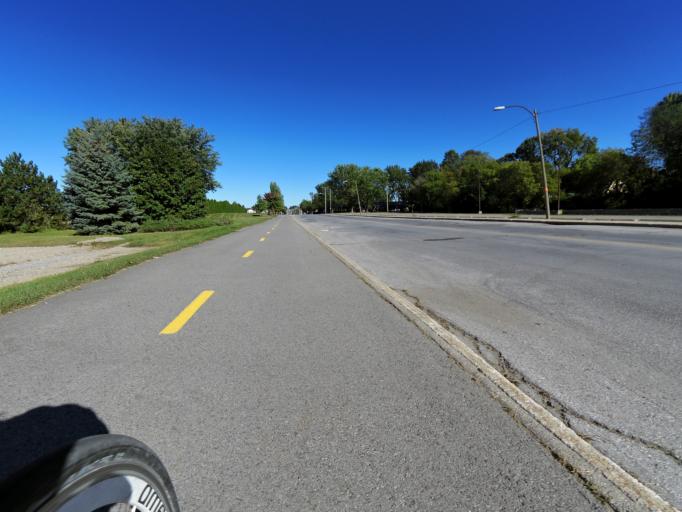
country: CA
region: Quebec
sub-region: Outaouais
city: Gatineau
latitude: 45.4802
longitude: -75.6507
